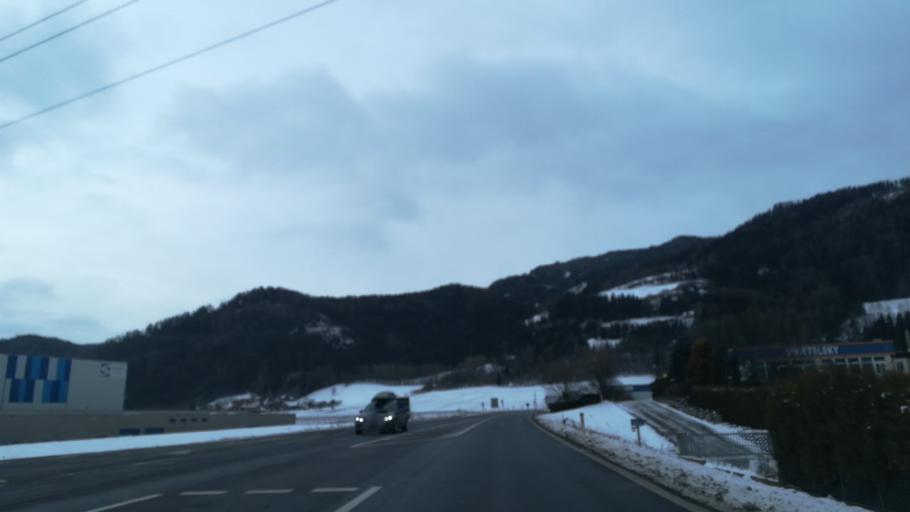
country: AT
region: Styria
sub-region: Politischer Bezirk Murtal
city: Sankt Peter ob Judenburg
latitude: 47.1849
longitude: 14.5992
